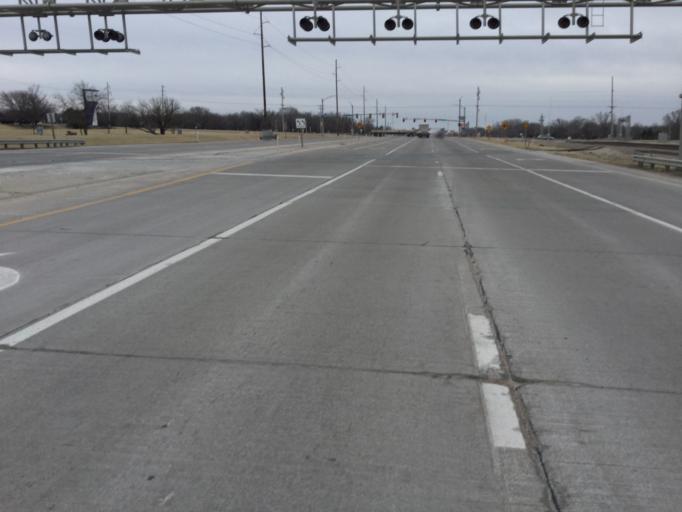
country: US
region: Kansas
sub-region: Sedgwick County
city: Derby
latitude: 37.6220
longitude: -97.2951
